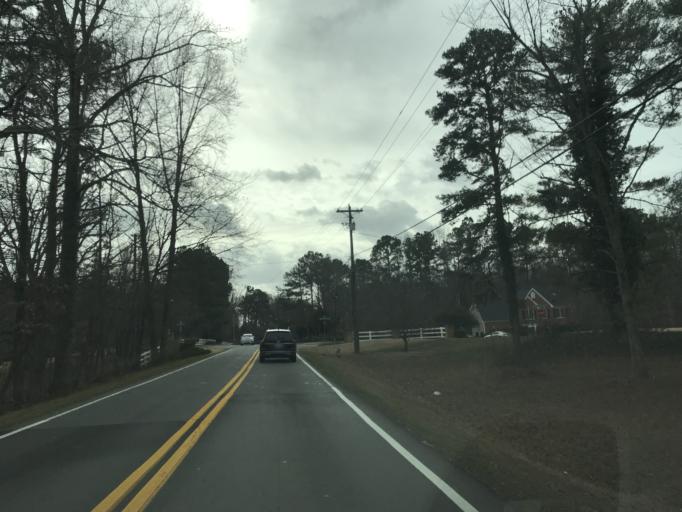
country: US
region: Georgia
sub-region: Fulton County
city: Milton
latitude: 34.1239
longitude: -84.2771
